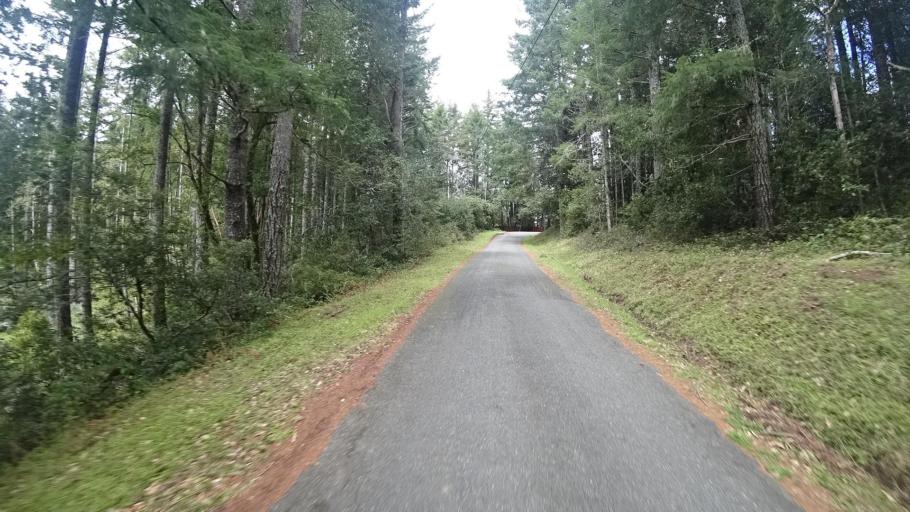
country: US
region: California
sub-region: Humboldt County
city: Blue Lake
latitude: 40.7975
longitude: -123.9850
